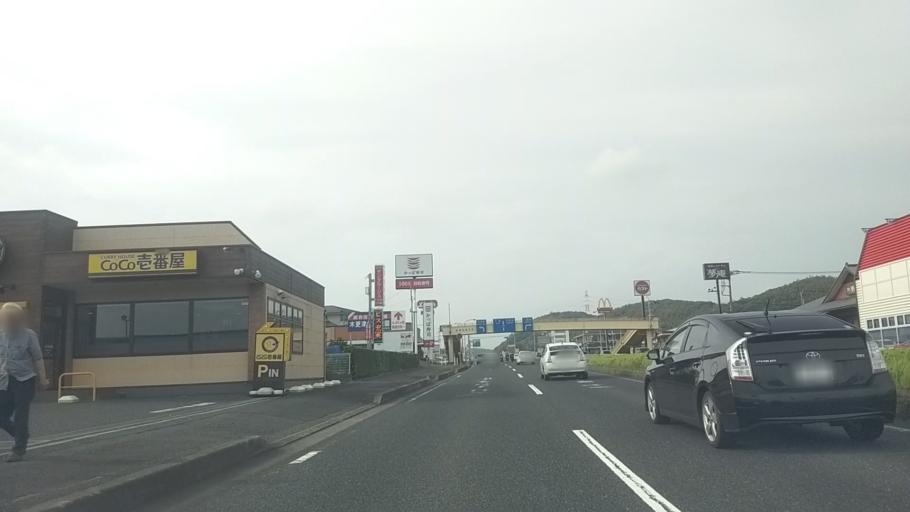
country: JP
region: Chiba
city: Kimitsu
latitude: 35.3277
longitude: 139.9241
